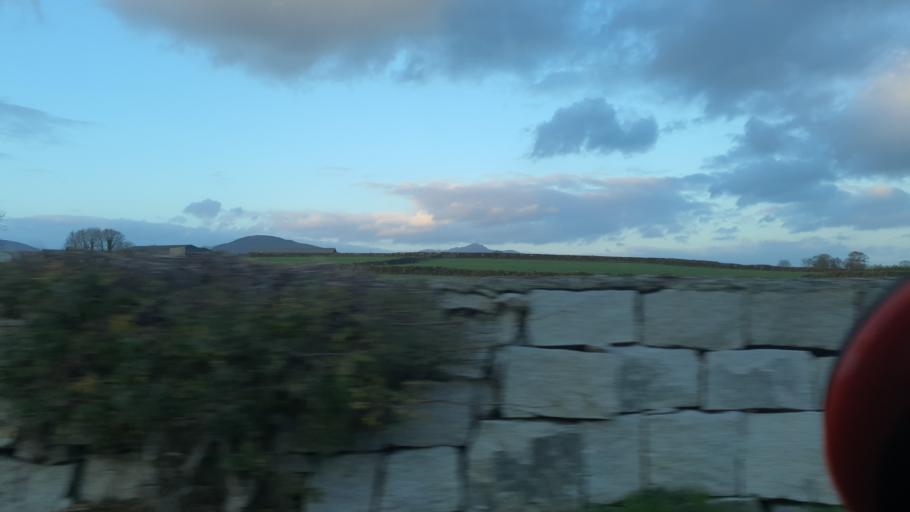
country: GB
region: Northern Ireland
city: Kilkeel
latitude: 54.0480
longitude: -6.0739
